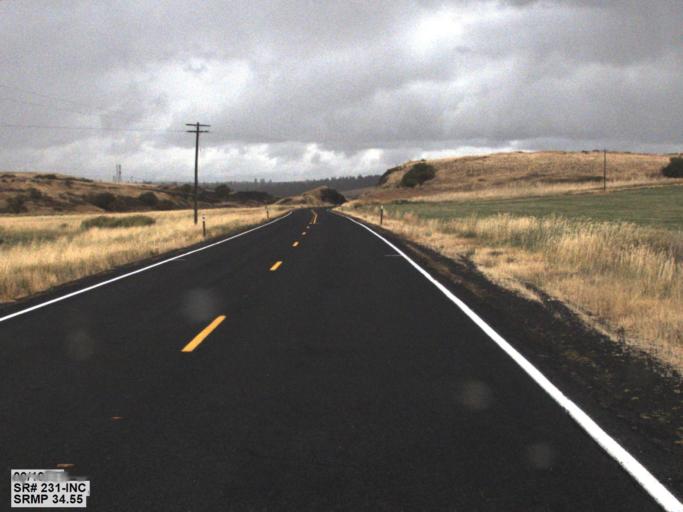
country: US
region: Washington
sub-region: Spokane County
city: Medical Lake
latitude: 47.7183
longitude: -117.8713
